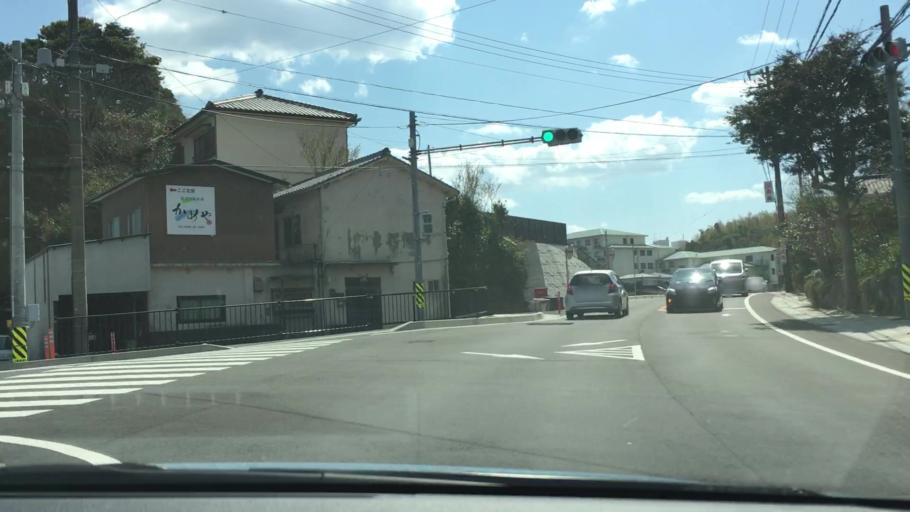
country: JP
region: Mie
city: Toba
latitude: 34.4615
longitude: 136.8635
